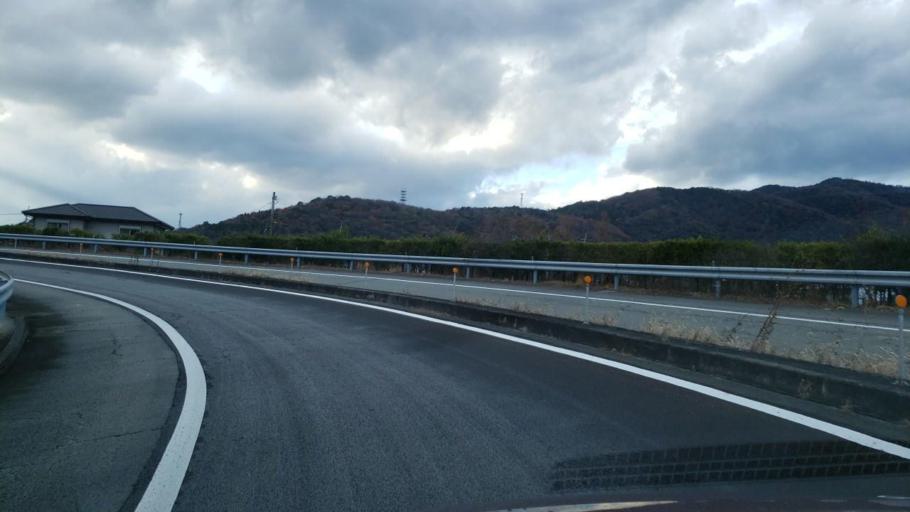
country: JP
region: Tokushima
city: Kamojimacho-jogejima
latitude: 34.1217
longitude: 134.3559
